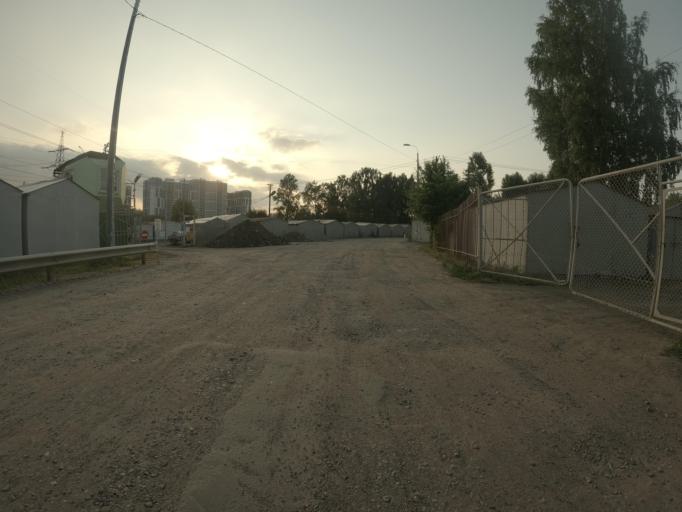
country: RU
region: St.-Petersburg
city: Krasnogvargeisky
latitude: 59.9554
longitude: 30.4569
